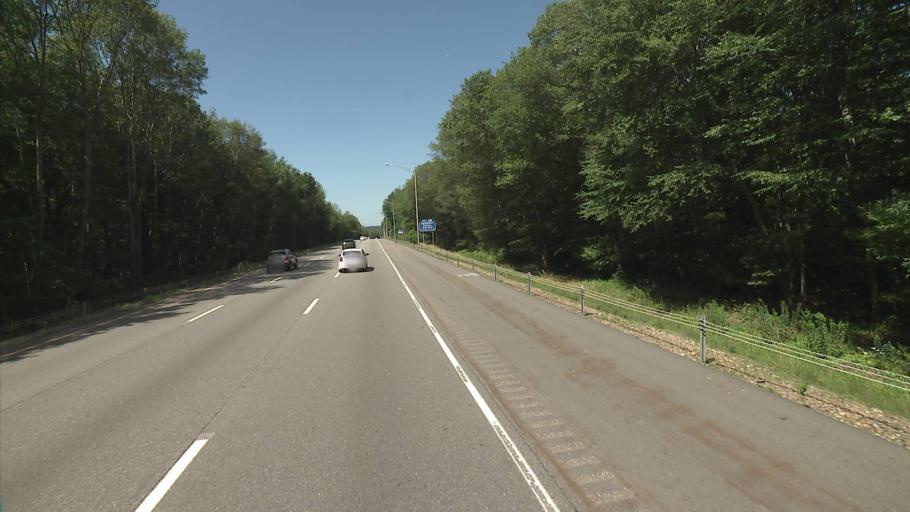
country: US
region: Connecticut
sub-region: New London County
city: Poquonock Bridge
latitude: 41.3653
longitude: -72.0162
